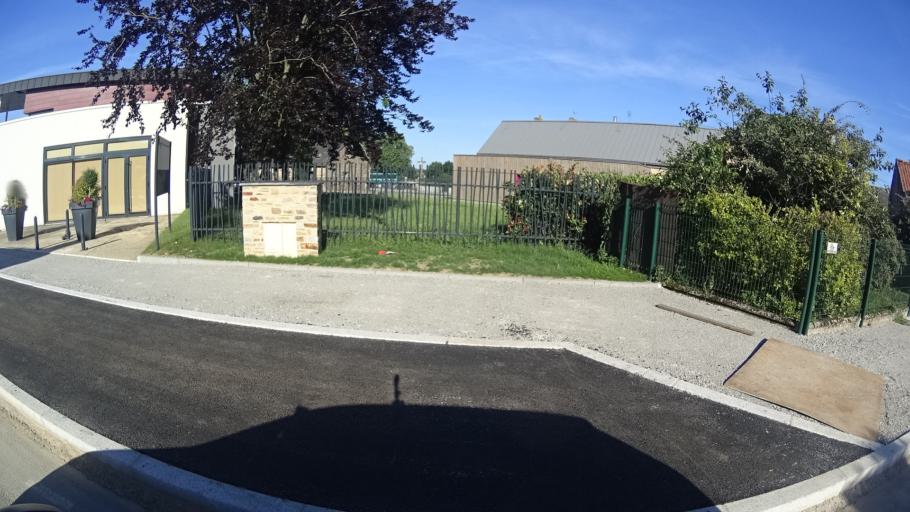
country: FR
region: Brittany
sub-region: Departement d'Ille-et-Vilaine
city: La Dominelais
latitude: 47.7618
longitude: -1.6880
